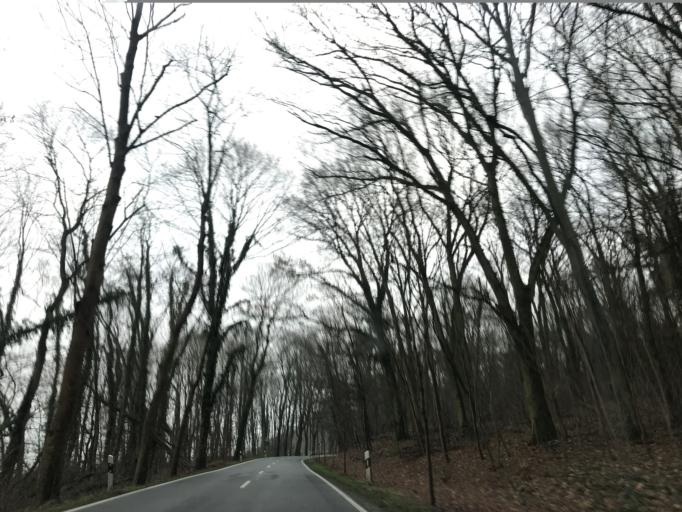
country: DE
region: Brandenburg
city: Kremmen
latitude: 52.7512
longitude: 12.9778
